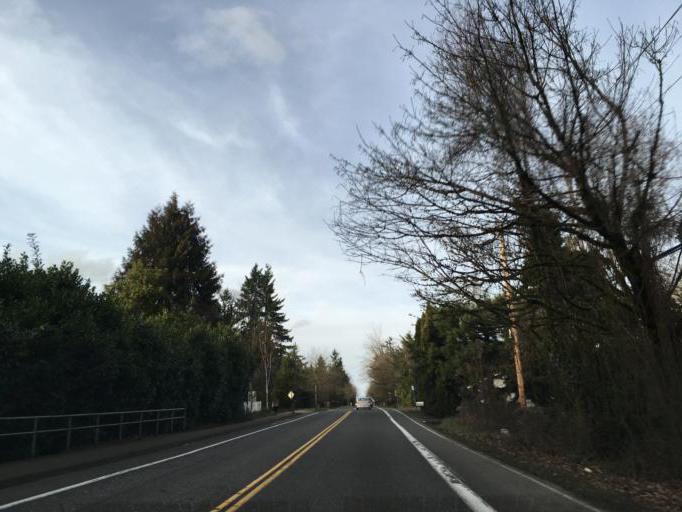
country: US
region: Oregon
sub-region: Clackamas County
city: Lake Oswego
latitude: 45.4567
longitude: -122.6850
